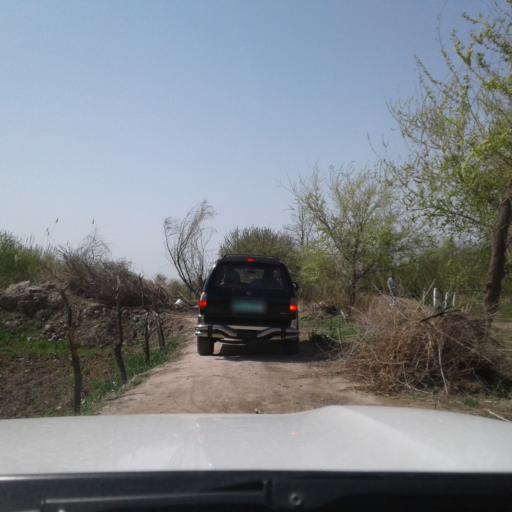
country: TM
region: Lebap
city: Turkmenabat
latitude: 38.9565
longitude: 63.6444
